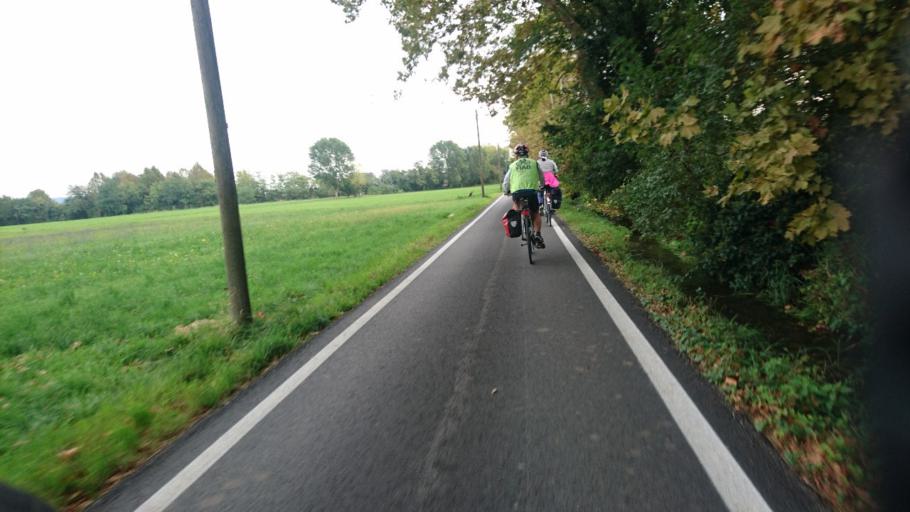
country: IT
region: Veneto
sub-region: Provincia di Verona
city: San Martino Buon Albergo
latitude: 45.4104
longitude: 11.1031
